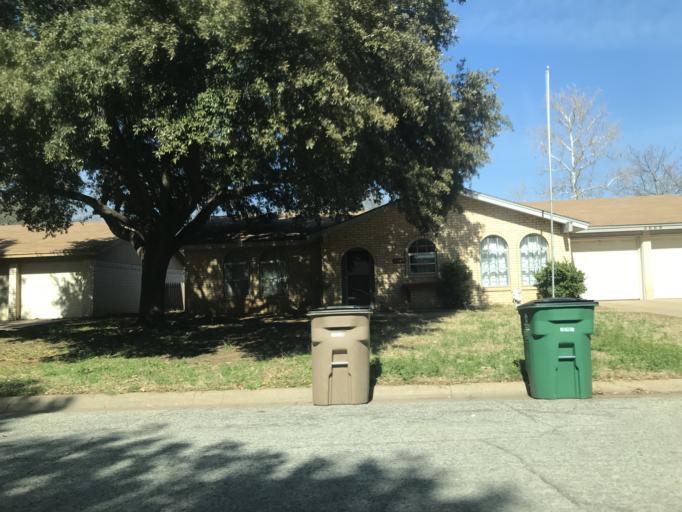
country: US
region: Texas
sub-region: Tom Green County
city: San Angelo
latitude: 31.4326
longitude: -100.4917
